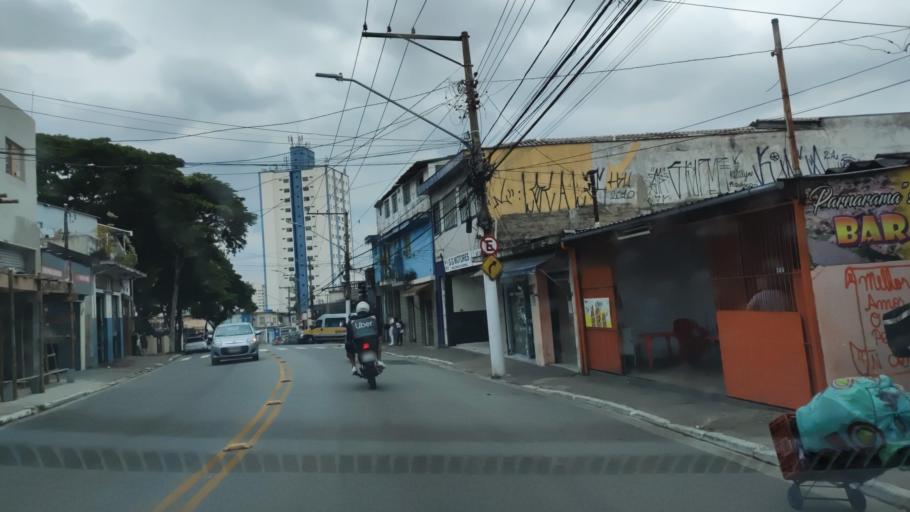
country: BR
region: Sao Paulo
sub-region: Sao Paulo
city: Sao Paulo
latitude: -23.4762
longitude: -46.6505
